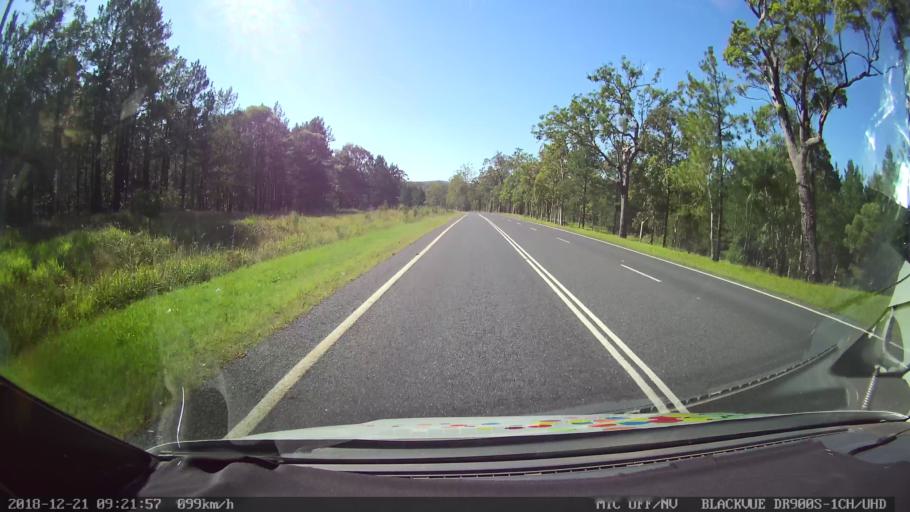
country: AU
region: New South Wales
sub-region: Clarence Valley
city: Maclean
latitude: -29.3360
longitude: 153.0013
